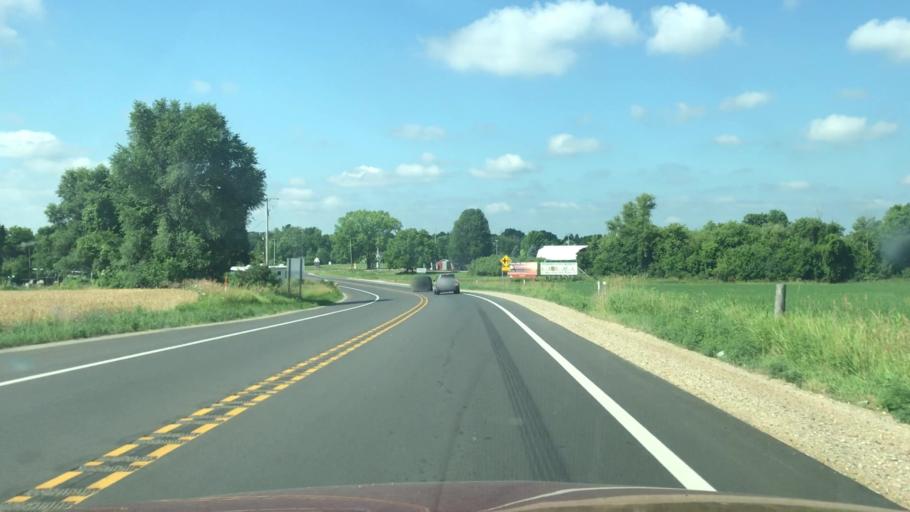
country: US
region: Michigan
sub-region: Newaygo County
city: Newaygo
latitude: 43.3531
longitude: -85.8095
